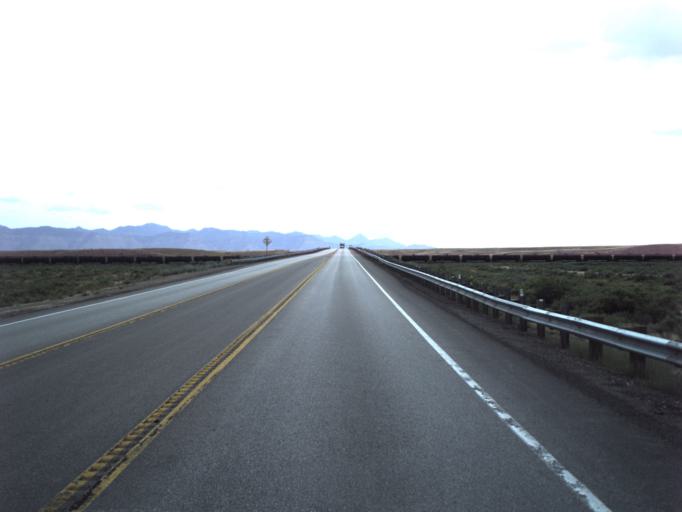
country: US
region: Utah
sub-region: Carbon County
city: East Carbon City
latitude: 39.5242
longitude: -110.5699
